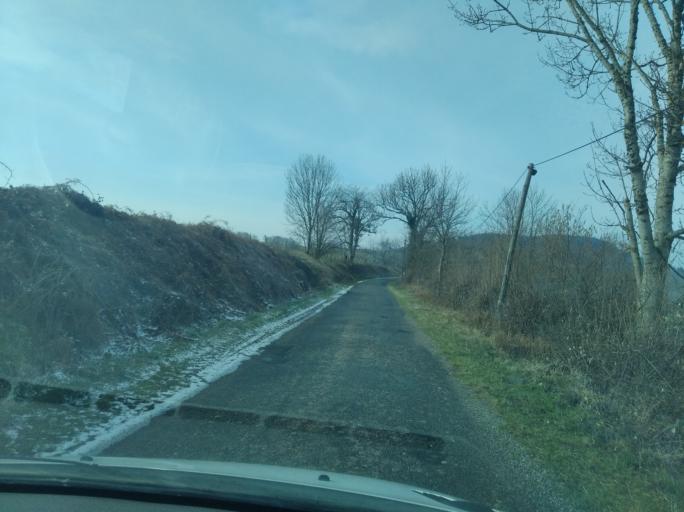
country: FR
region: Rhone-Alpes
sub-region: Departement de la Loire
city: La Pacaudiere
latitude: 46.1390
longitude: 3.7632
